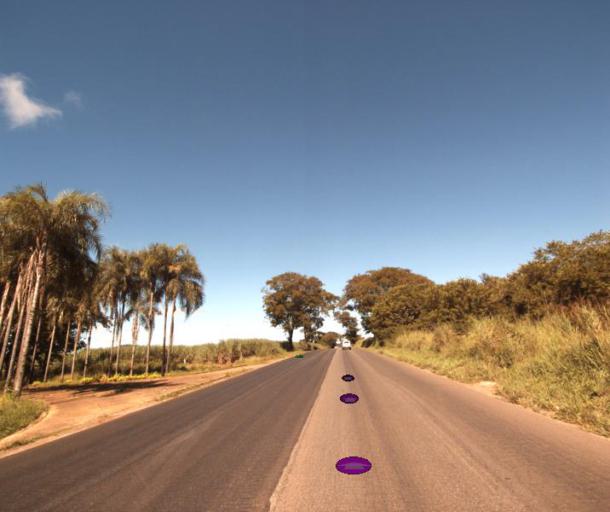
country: BR
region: Goias
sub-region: Itapaci
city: Itapaci
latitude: -15.1295
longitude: -49.5117
